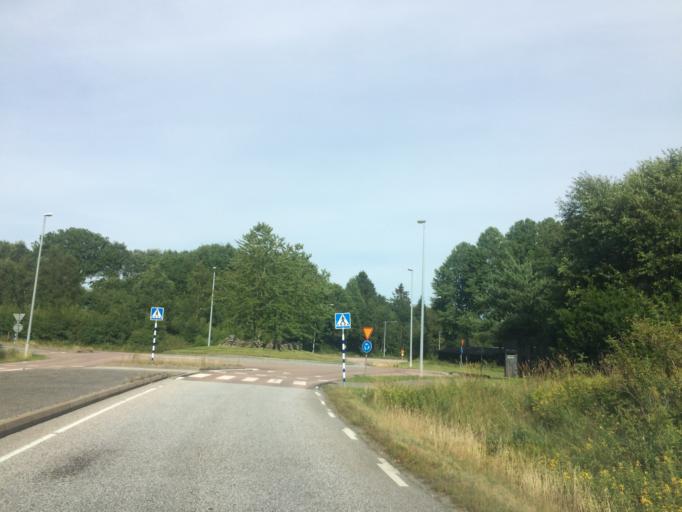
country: SE
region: Vaestra Goetaland
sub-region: Partille Kommun
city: Ojersjo
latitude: 57.6996
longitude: 12.1321
